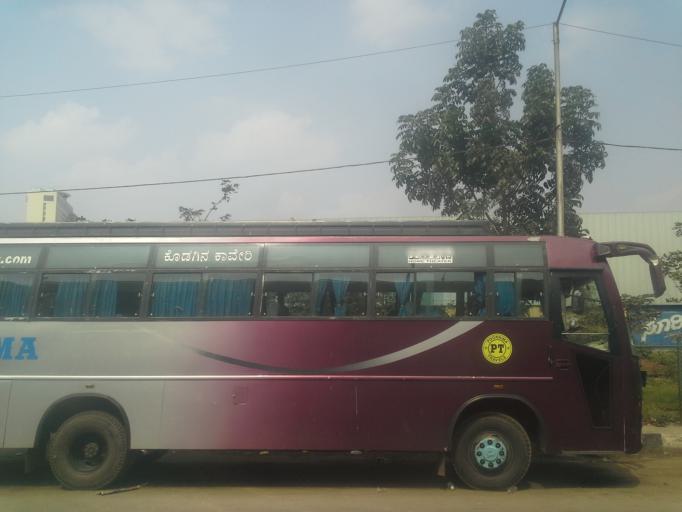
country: IN
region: Karnataka
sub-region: Bangalore Urban
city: Bangalore
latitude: 12.9807
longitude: 77.5777
